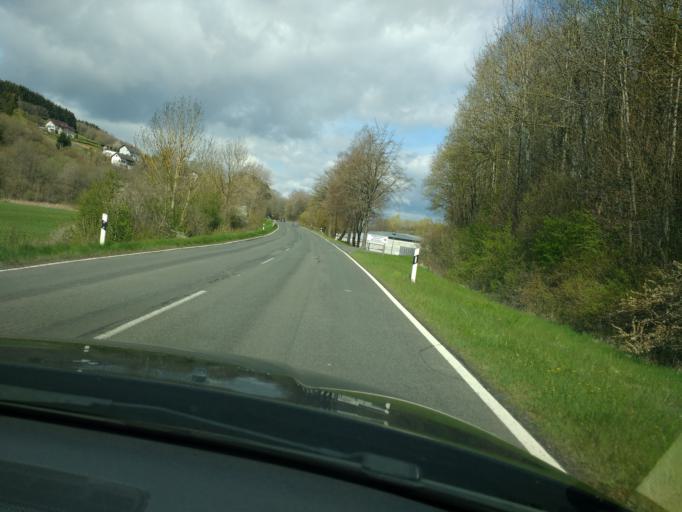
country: DE
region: Rheinland-Pfalz
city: Gonnersdorf
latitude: 50.3315
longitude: 6.6038
